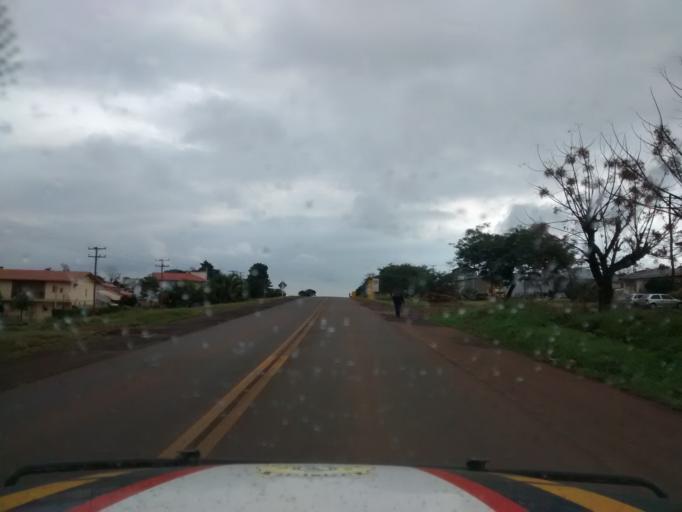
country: BR
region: Rio Grande do Sul
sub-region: Lagoa Vermelha
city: Lagoa Vermelha
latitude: -28.2066
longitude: -51.5166
